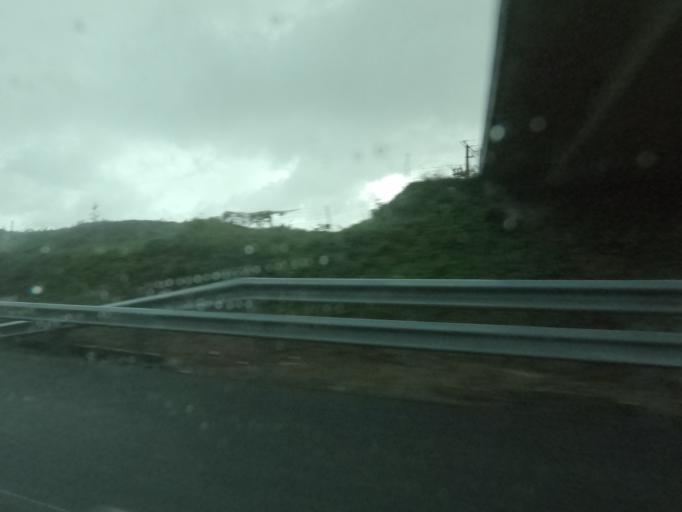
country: ES
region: Galicia
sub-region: Provincia de Pontevedra
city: Marin
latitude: 42.3613
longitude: -8.6401
